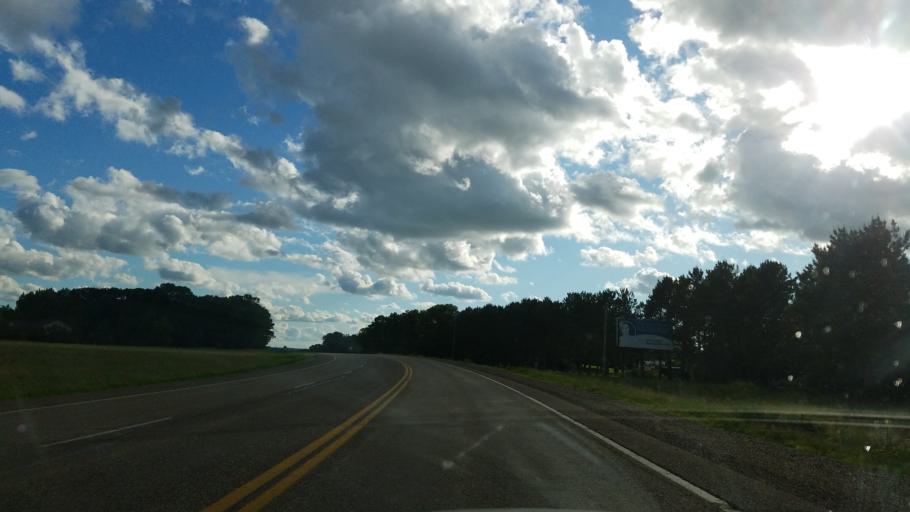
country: US
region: Wisconsin
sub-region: Polk County
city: Osceola
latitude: 45.3431
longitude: -92.6676
